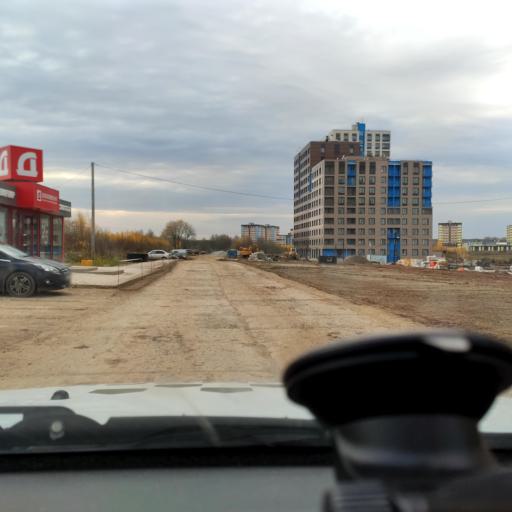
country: RU
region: Perm
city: Perm
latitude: 58.0104
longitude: 56.3329
